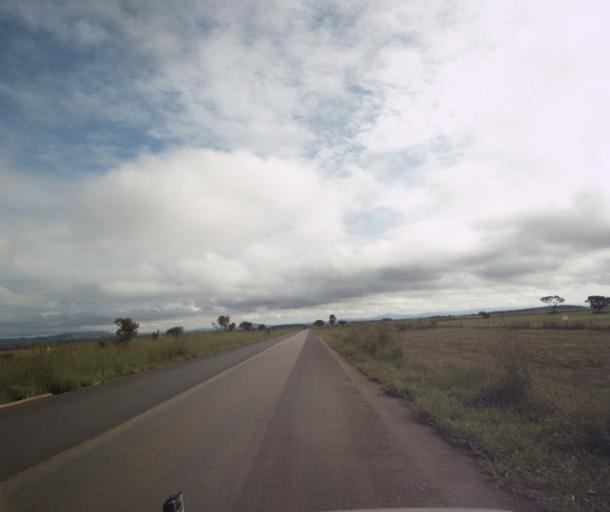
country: BR
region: Goias
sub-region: Padre Bernardo
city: Padre Bernardo
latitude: -15.3560
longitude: -48.6466
